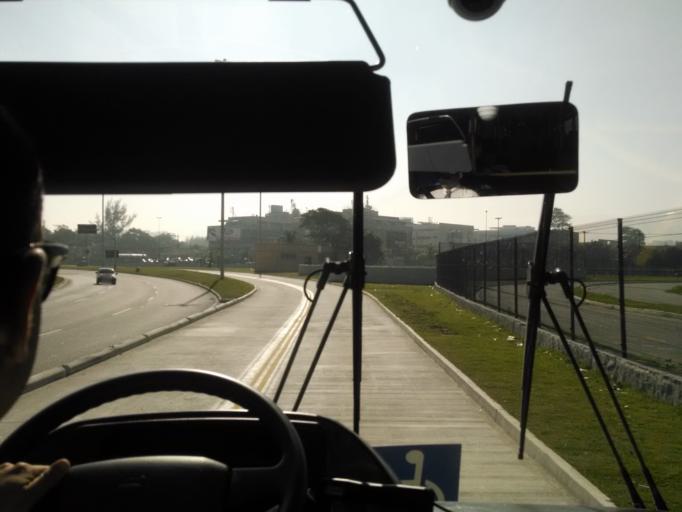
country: BR
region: Rio de Janeiro
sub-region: Rio De Janeiro
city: Rio de Janeiro
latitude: -22.9977
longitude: -43.3666
